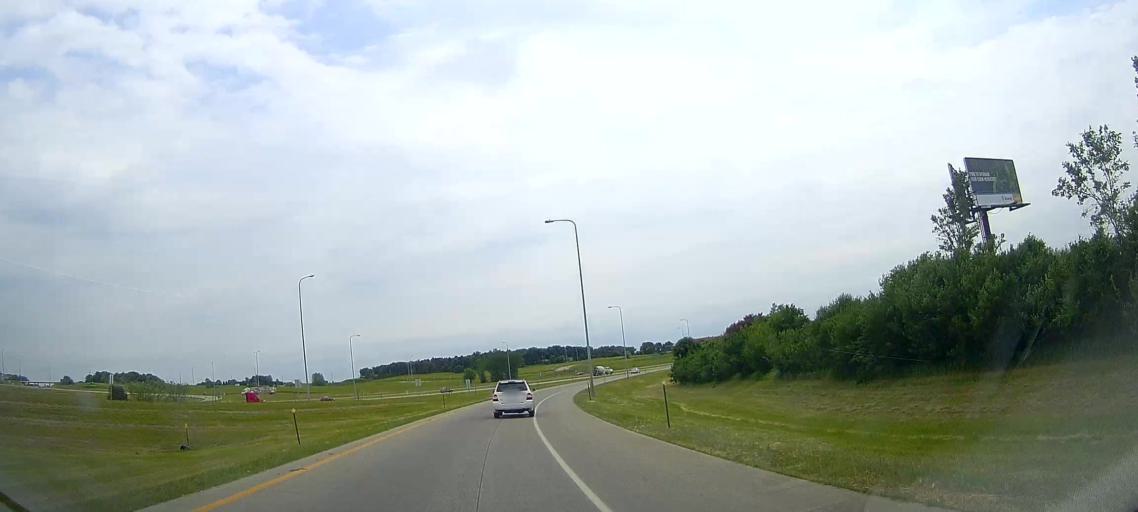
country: US
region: South Dakota
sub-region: Minnehaha County
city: Crooks
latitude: 43.6117
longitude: -96.7727
